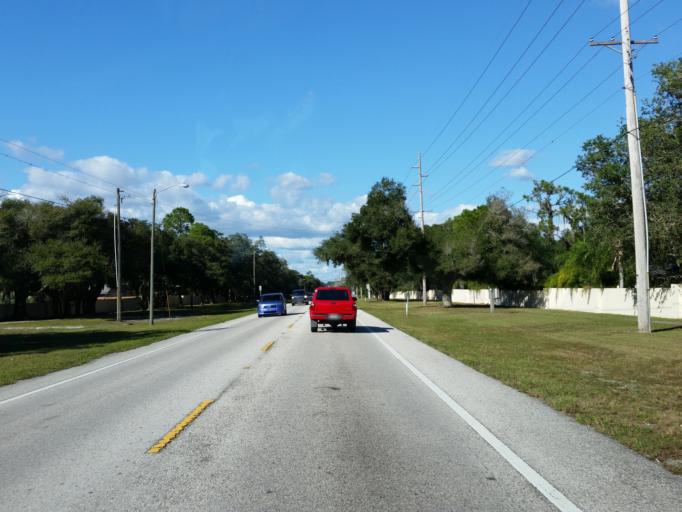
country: US
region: Florida
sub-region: Hillsborough County
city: Bloomingdale
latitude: 27.8819
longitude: -82.2693
